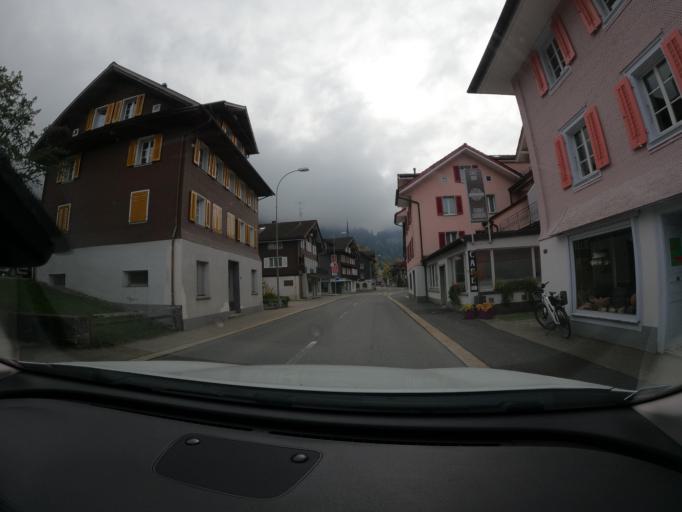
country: CH
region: Obwalden
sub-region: Obwalden
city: Lungern
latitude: 46.7854
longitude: 8.1596
